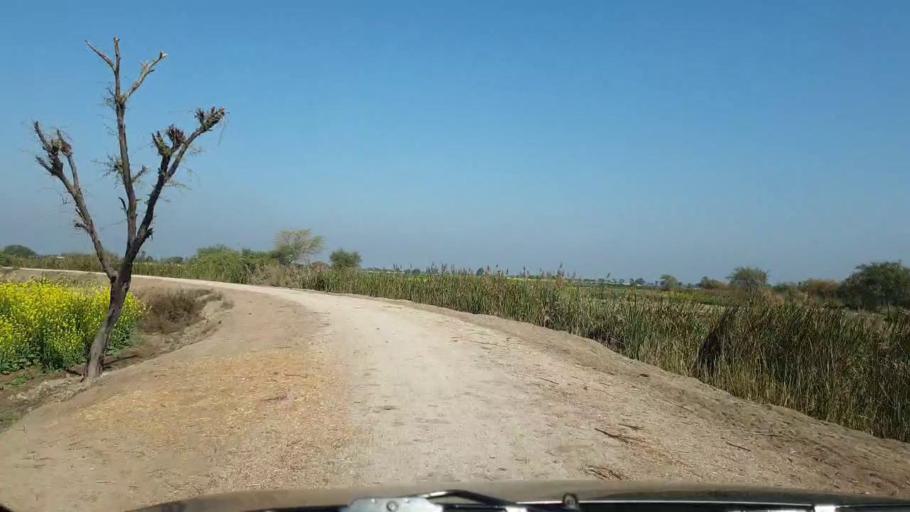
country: PK
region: Sindh
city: Sinjhoro
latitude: 25.9704
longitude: 68.7530
